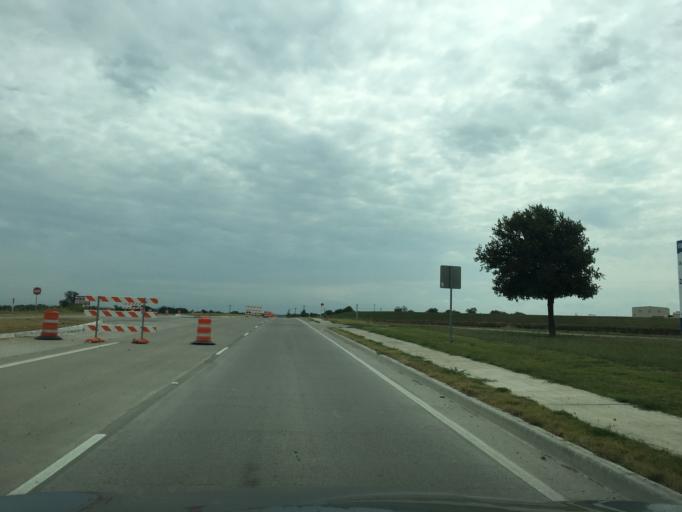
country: US
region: Texas
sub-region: Collin County
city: Melissa
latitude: 33.3010
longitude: -96.5315
